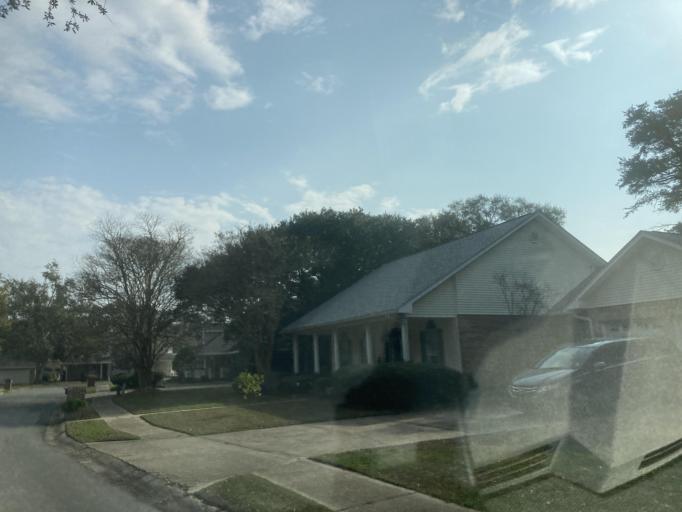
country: US
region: Mississippi
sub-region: Harrison County
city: Long Beach
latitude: 30.3548
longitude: -89.1889
